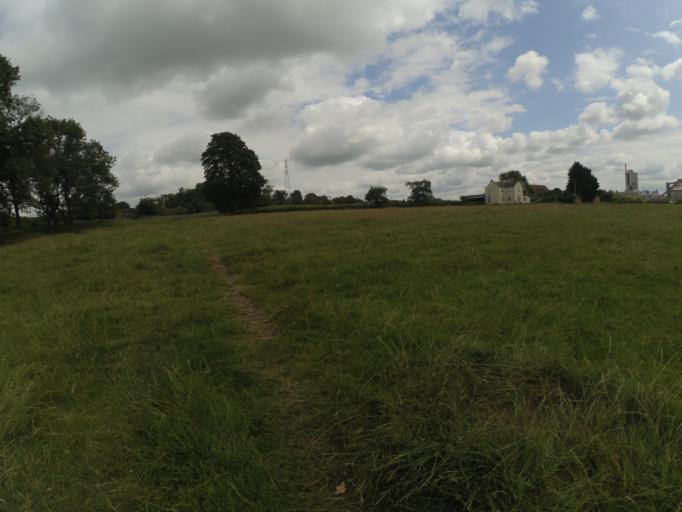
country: GB
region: England
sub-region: Warwickshire
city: Long Lawford
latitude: 52.3862
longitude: -1.2936
